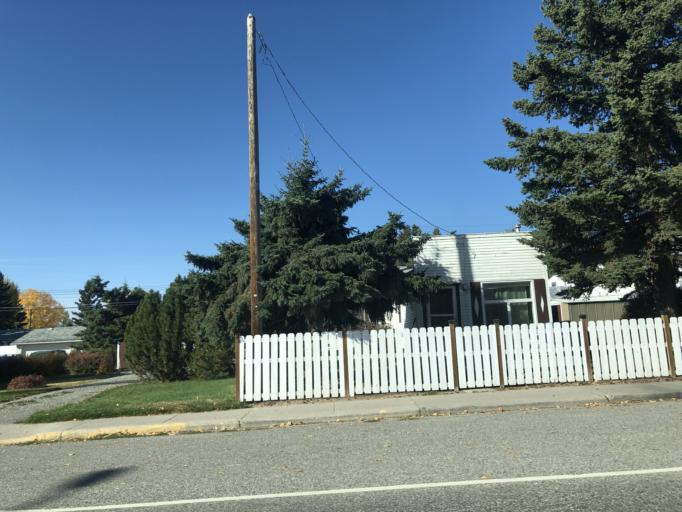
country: CA
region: Alberta
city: Black Diamond
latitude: 50.5316
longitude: -114.2310
